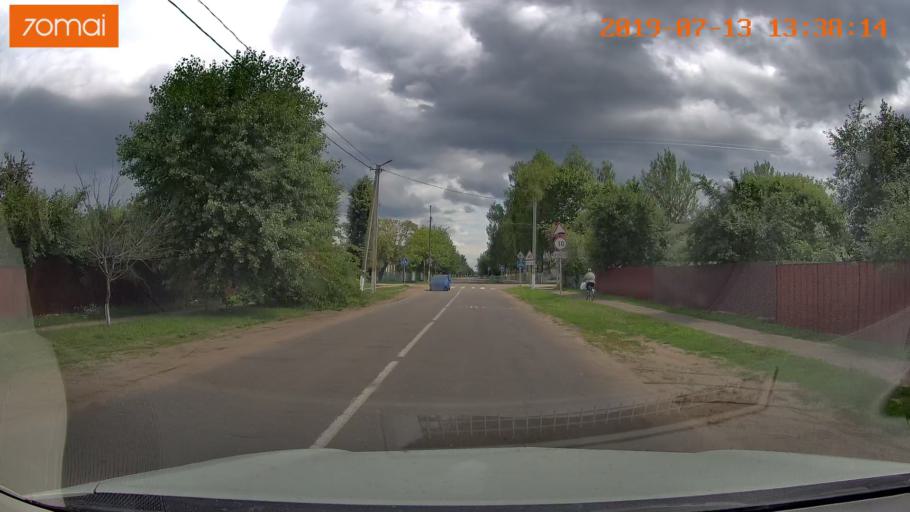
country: BY
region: Mogilev
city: Asipovichy
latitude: 53.2986
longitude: 28.6327
